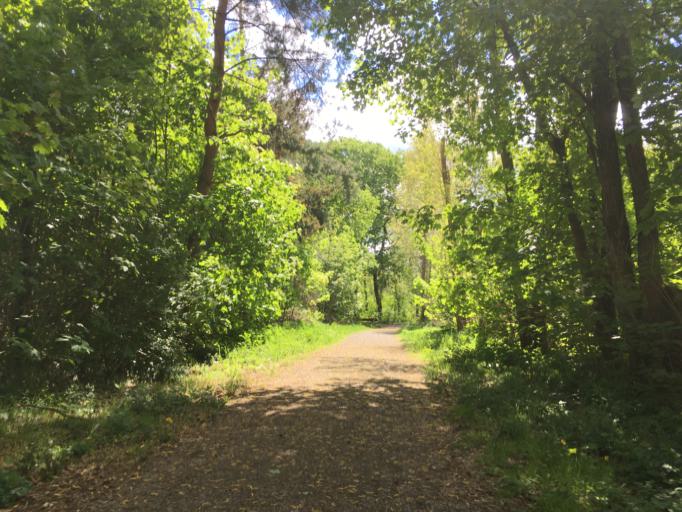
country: DE
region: Berlin
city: Blankenfelde
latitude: 52.6269
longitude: 13.3897
